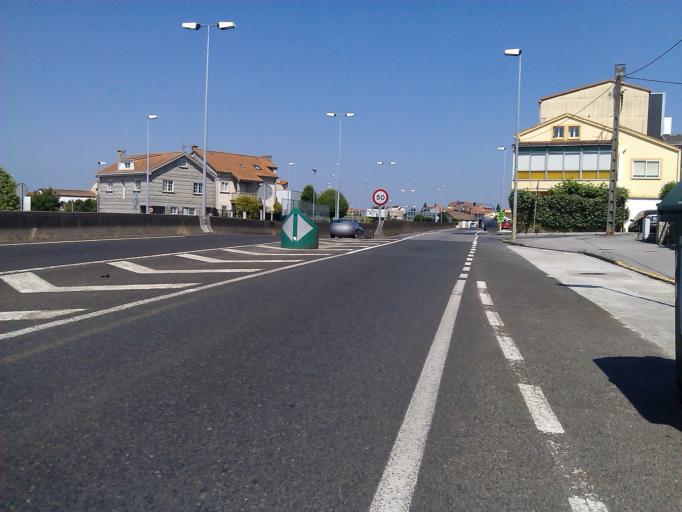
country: ES
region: Galicia
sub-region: Provincia da Coruna
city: Santiago de Compostela
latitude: 42.8589
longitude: -8.5382
